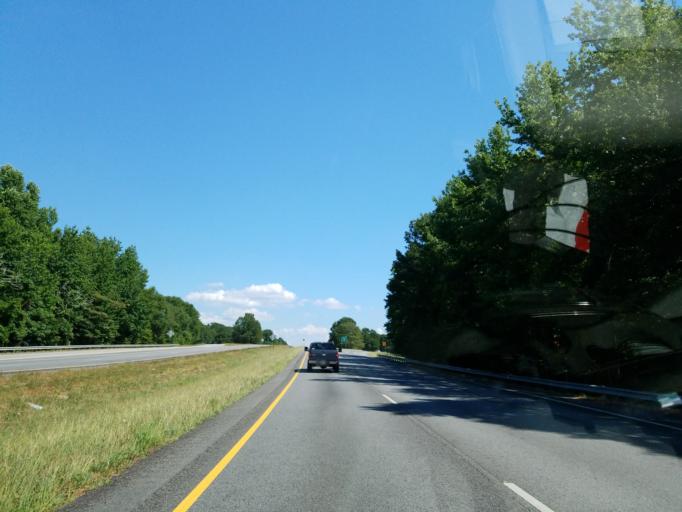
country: US
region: Georgia
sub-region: Spalding County
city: Griffin
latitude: 33.2335
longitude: -84.2940
